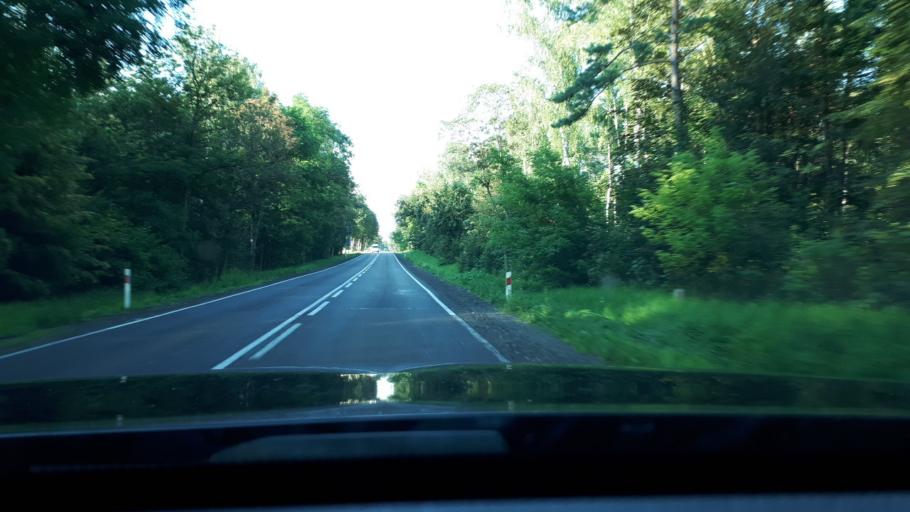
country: PL
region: Masovian Voivodeship
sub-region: Powiat ciechanowski
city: Ojrzen
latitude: 52.7848
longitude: 20.5620
